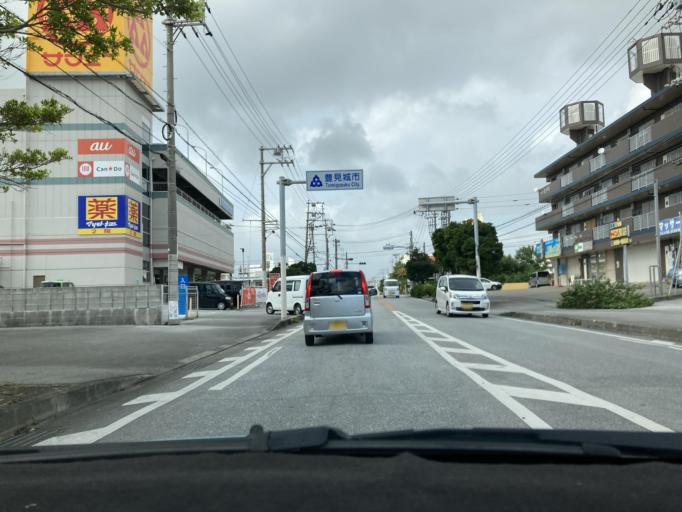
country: JP
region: Okinawa
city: Itoman
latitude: 26.1531
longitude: 127.6717
